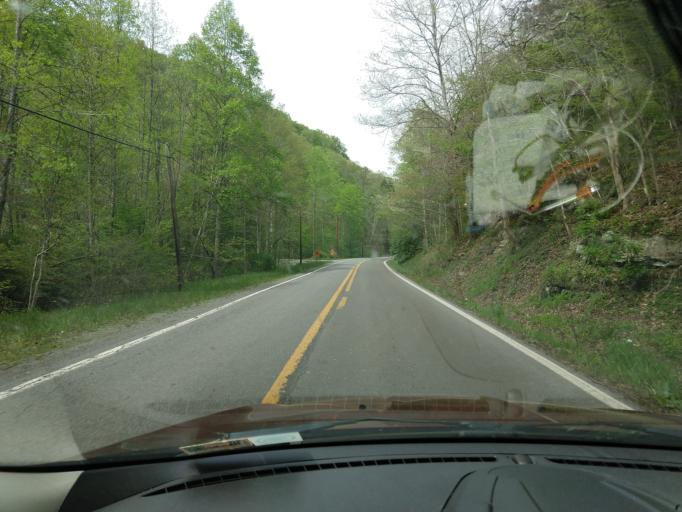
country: US
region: West Virginia
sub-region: McDowell County
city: Welch
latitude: 37.3501
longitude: -81.6667
